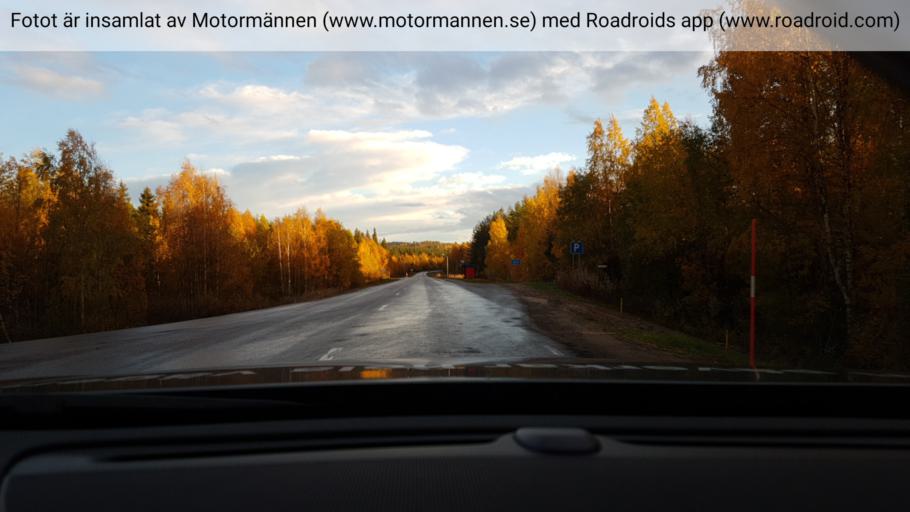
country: SE
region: Norrbotten
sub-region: Overkalix Kommun
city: OEverkalix
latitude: 66.6111
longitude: 22.7570
